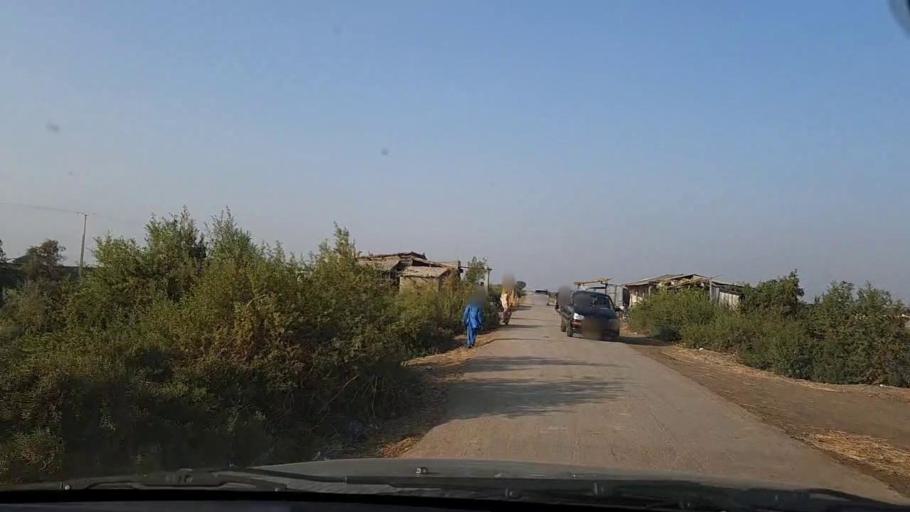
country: PK
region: Sindh
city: Chuhar Jamali
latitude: 24.3028
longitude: 67.7555
